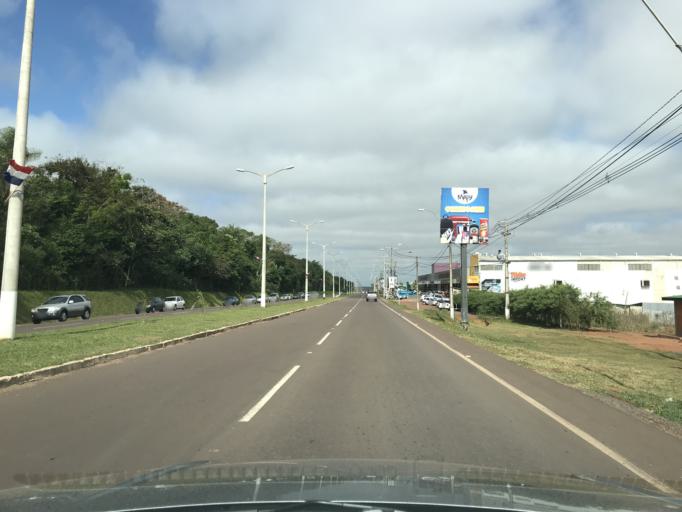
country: PY
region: Canindeyu
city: Salto del Guaira
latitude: -24.0116
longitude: -54.3245
